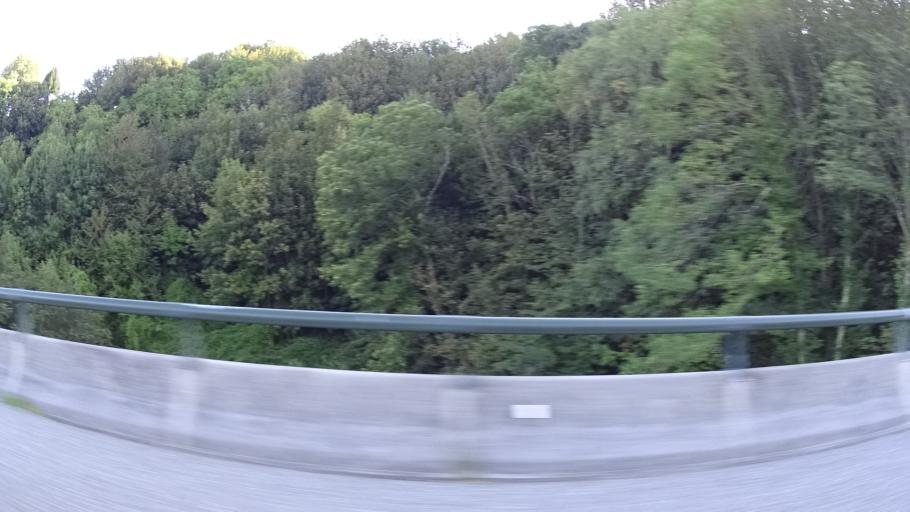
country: ES
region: Galicia
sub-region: Provincia de Lugo
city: San Roman
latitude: 42.7590
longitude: -7.0756
